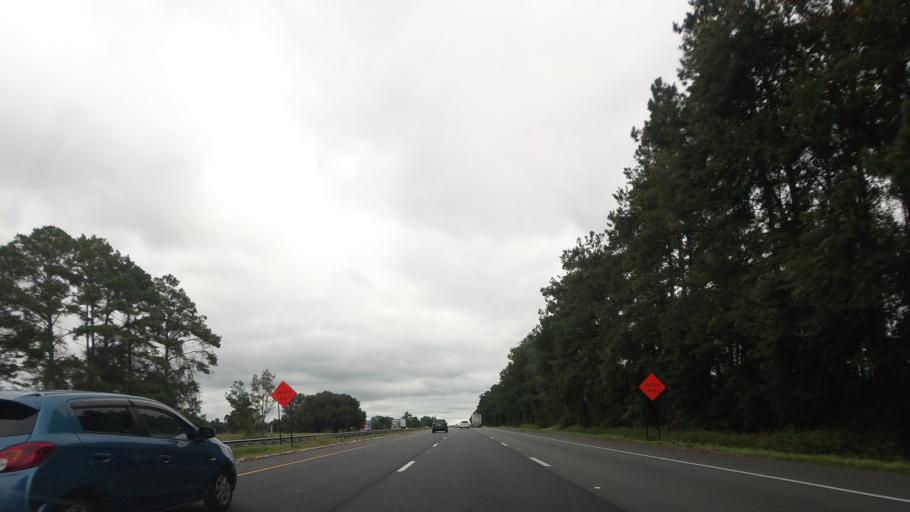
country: US
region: Florida
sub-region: Alachua County
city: High Springs
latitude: 29.9230
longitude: -82.5573
